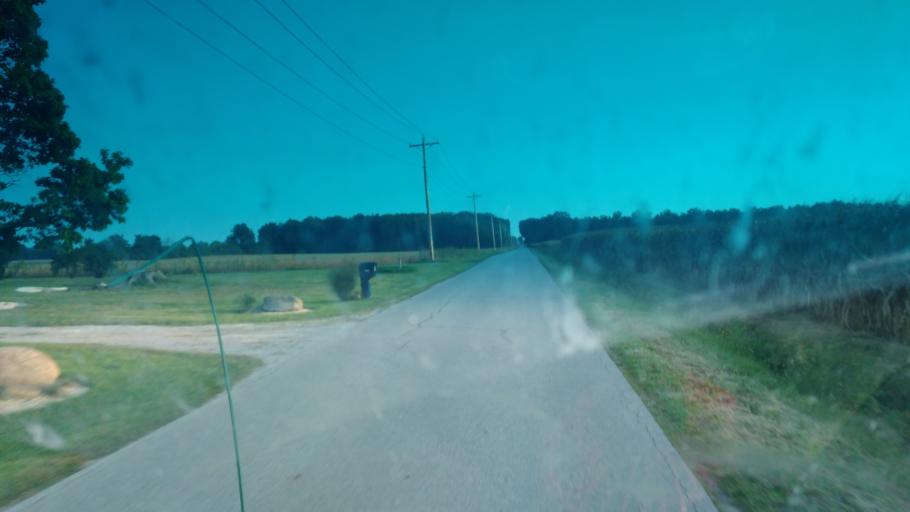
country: US
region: Ohio
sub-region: Crawford County
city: Galion
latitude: 40.7988
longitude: -82.8191
